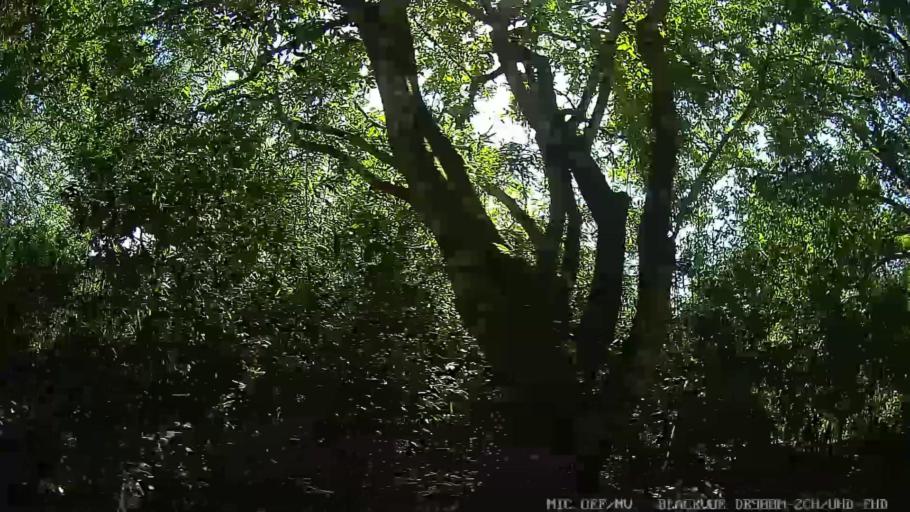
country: BR
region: Sao Paulo
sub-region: Itanhaem
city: Itanhaem
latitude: -24.2327
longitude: -46.8781
